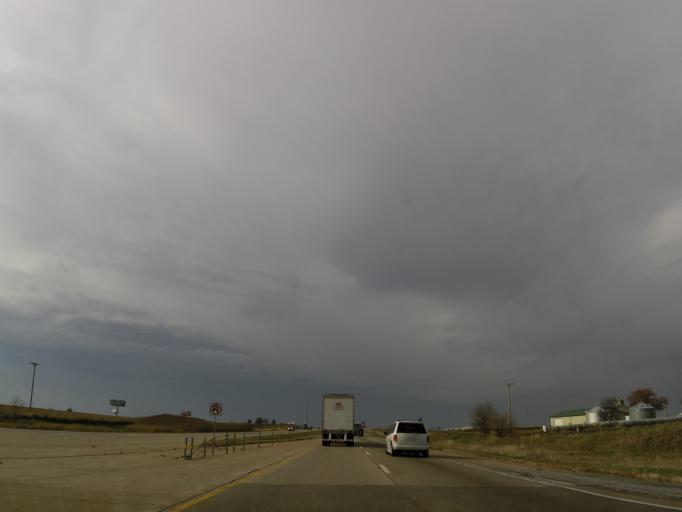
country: US
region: Iowa
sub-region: Scott County
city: Walcott
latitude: 41.6124
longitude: -90.7621
